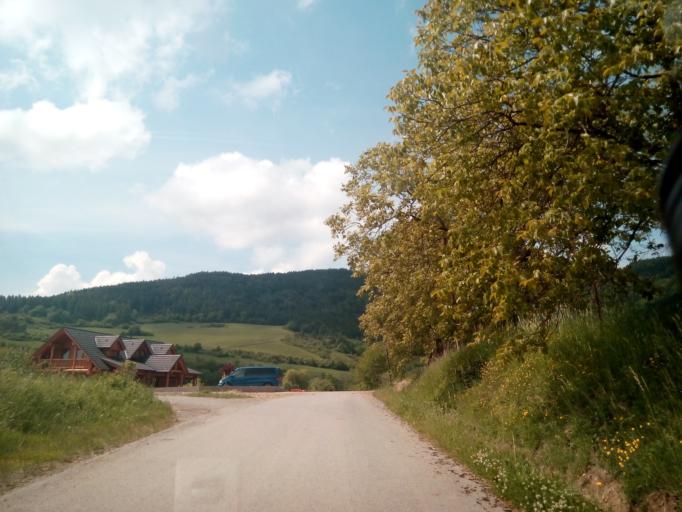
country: SK
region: Presovsky
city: Lipany
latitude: 49.0616
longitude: 20.9501
